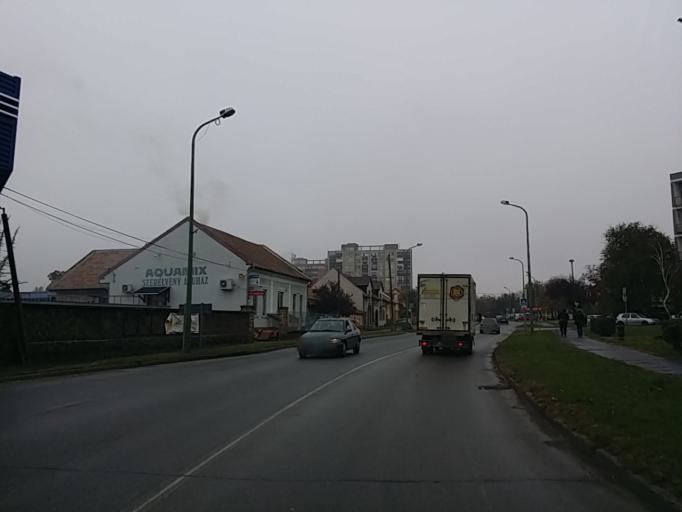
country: HU
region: Heves
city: Gyongyos
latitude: 47.7733
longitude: 19.9215
